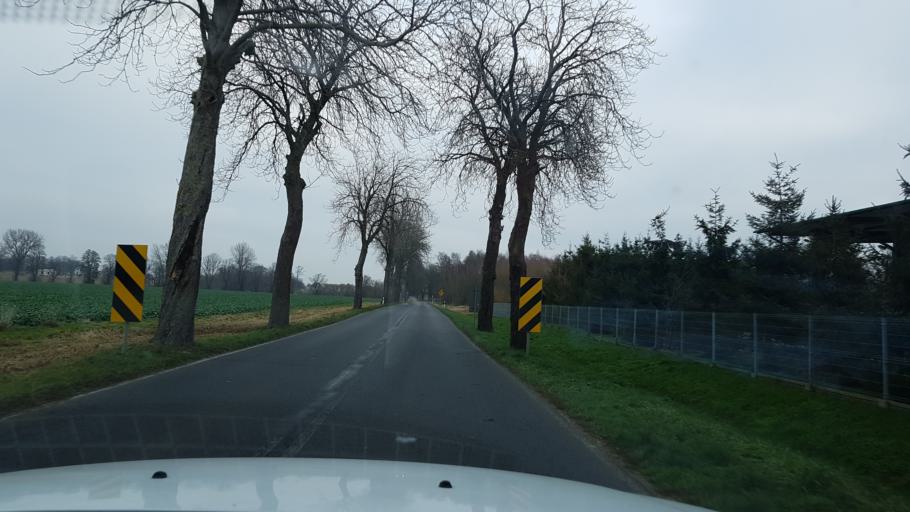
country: PL
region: West Pomeranian Voivodeship
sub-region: Powiat gryficki
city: Trzebiatow
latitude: 54.0686
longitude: 15.2428
